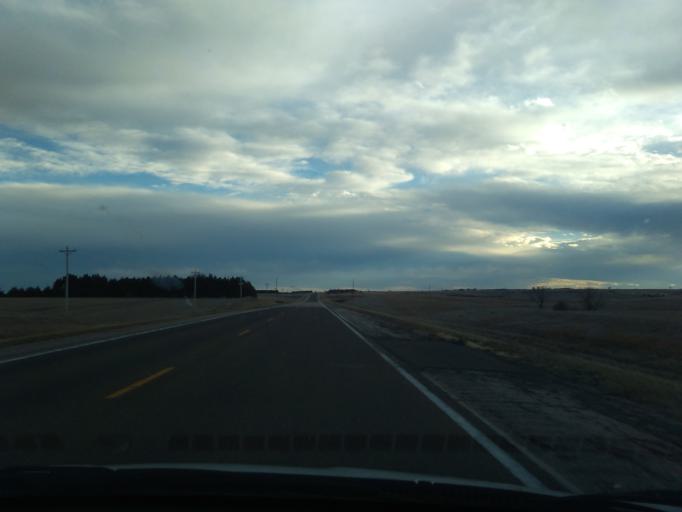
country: US
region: Nebraska
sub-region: Phelps County
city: Holdrege
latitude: 40.3423
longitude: -99.3687
